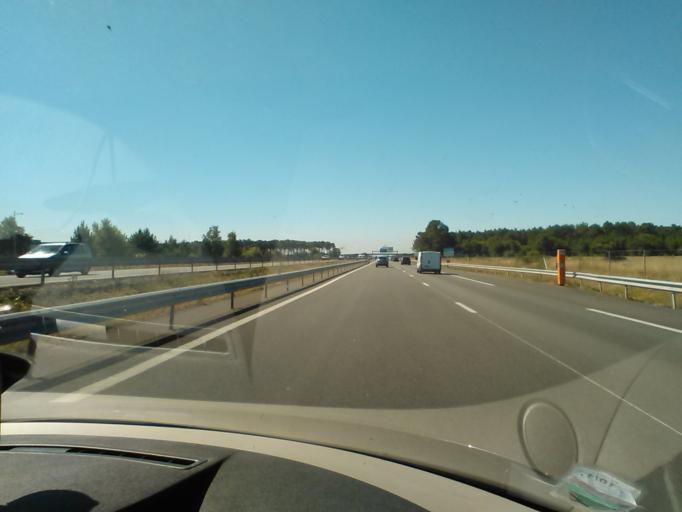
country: FR
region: Aquitaine
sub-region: Departement des Landes
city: Saint-Geours-de-Maremne
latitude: 43.7188
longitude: -1.2278
